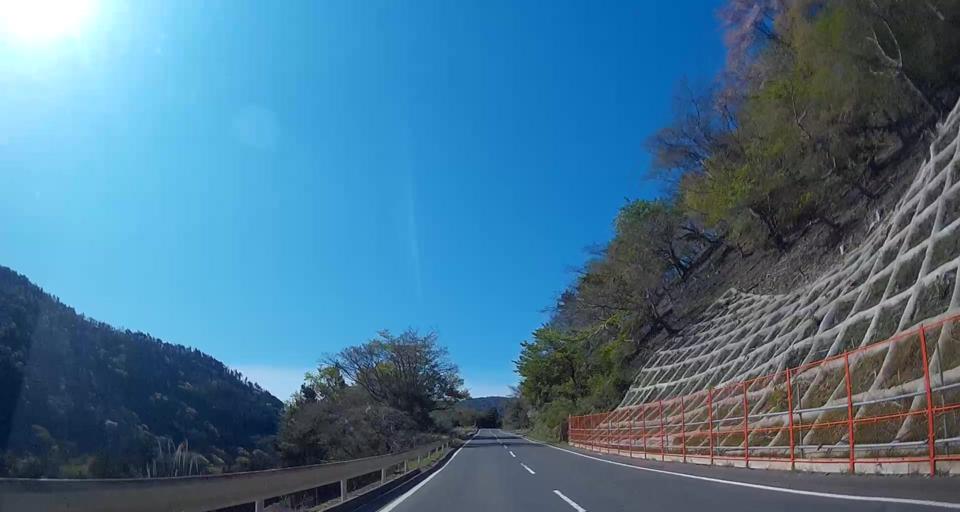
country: JP
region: Miyagi
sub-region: Oshika Gun
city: Onagawa Cho
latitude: 38.4322
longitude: 141.4474
